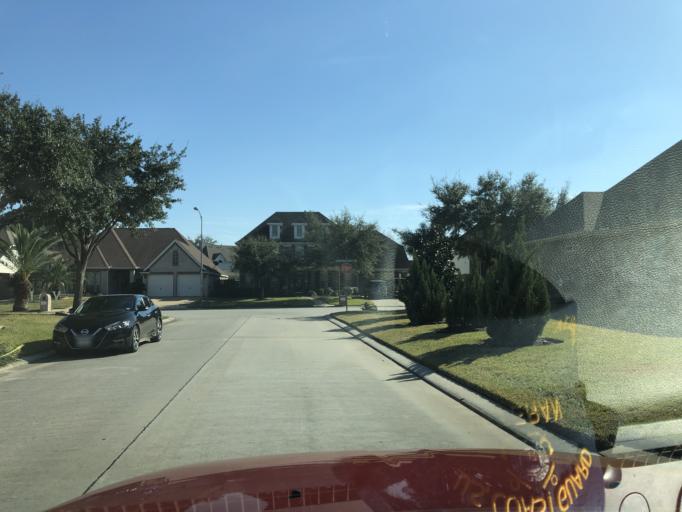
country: US
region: Texas
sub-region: Harris County
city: Tomball
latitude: 30.0342
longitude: -95.5502
